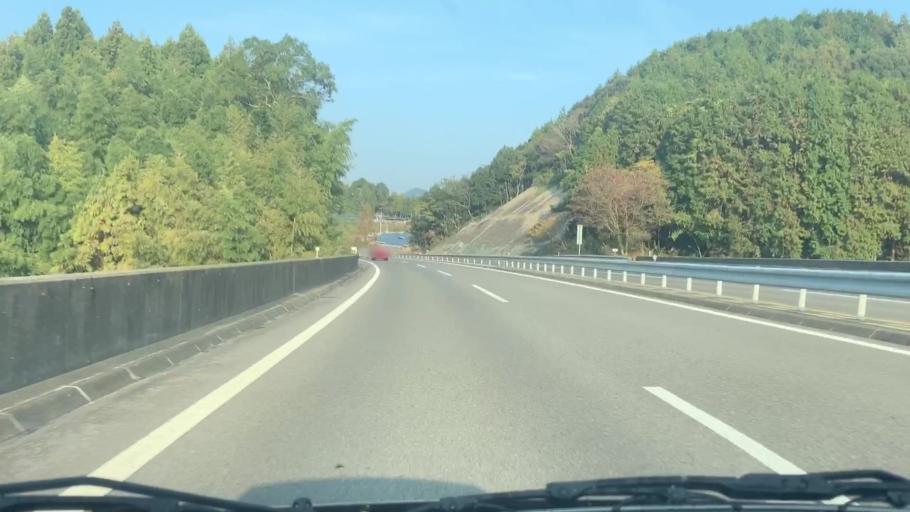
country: JP
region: Saga Prefecture
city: Ureshinomachi-shimojuku
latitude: 33.1527
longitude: 129.9338
